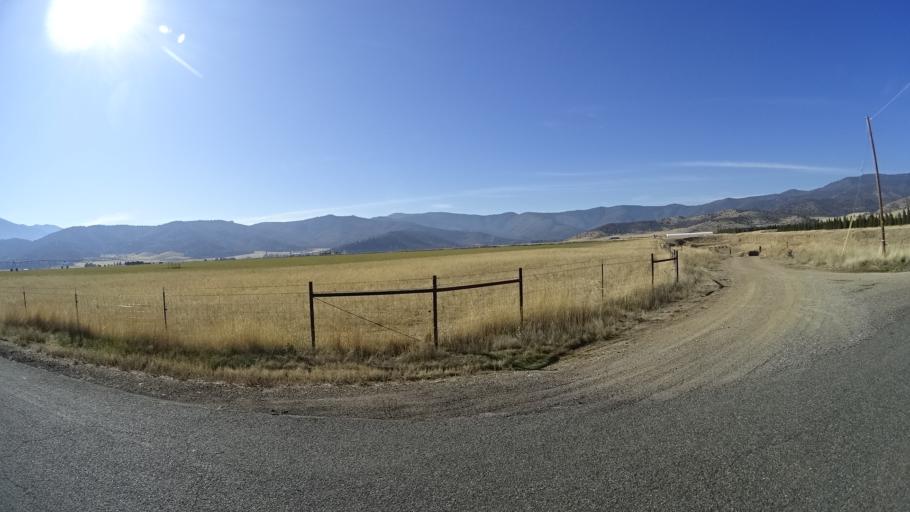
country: US
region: California
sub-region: Siskiyou County
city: Montague
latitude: 41.5506
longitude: -122.5439
